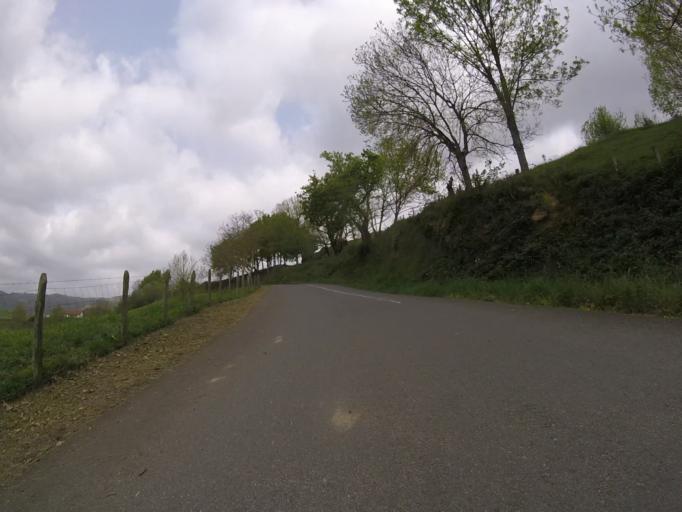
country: ES
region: Basque Country
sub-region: Provincia de Guipuzcoa
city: Zizurkil
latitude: 43.2040
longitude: -2.0759
